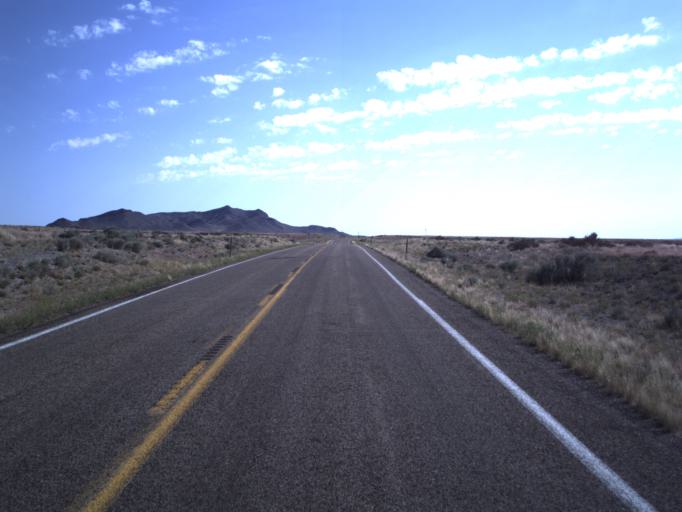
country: US
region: Utah
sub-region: Beaver County
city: Milford
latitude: 38.7820
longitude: -112.9227
